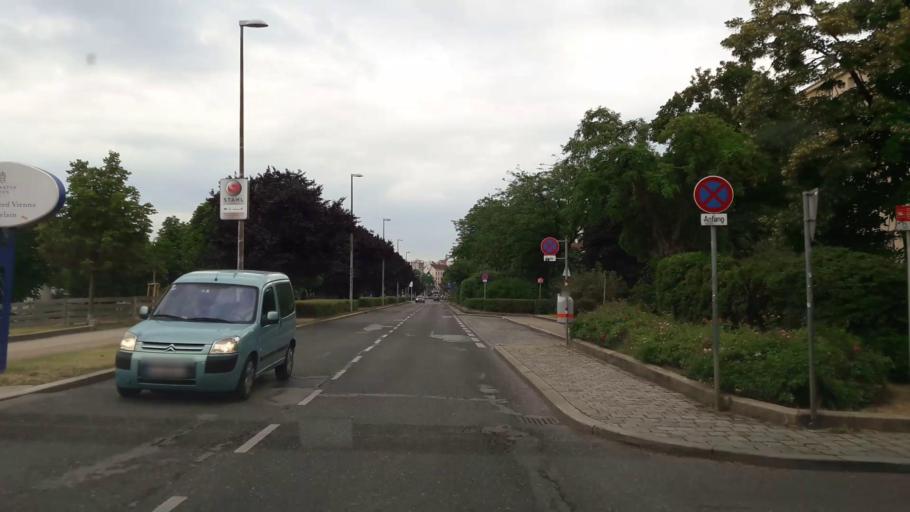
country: AT
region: Vienna
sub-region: Wien Stadt
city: Vienna
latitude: 48.2221
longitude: 16.3765
